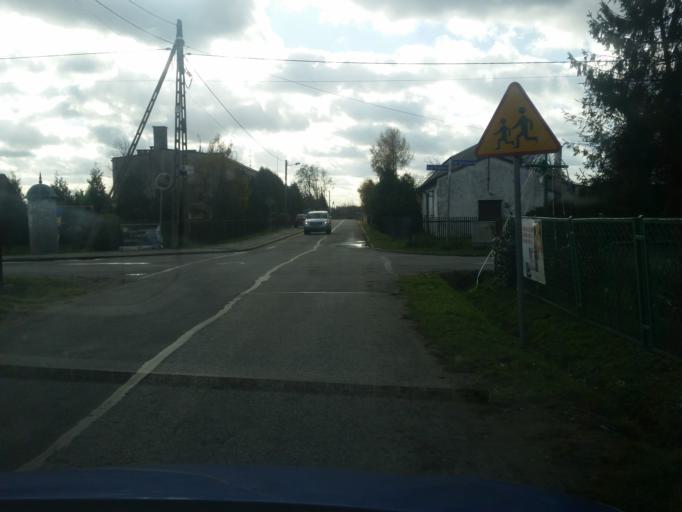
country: PL
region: Silesian Voivodeship
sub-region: Powiat czestochowski
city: Klomnice
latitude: 50.9614
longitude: 19.3273
